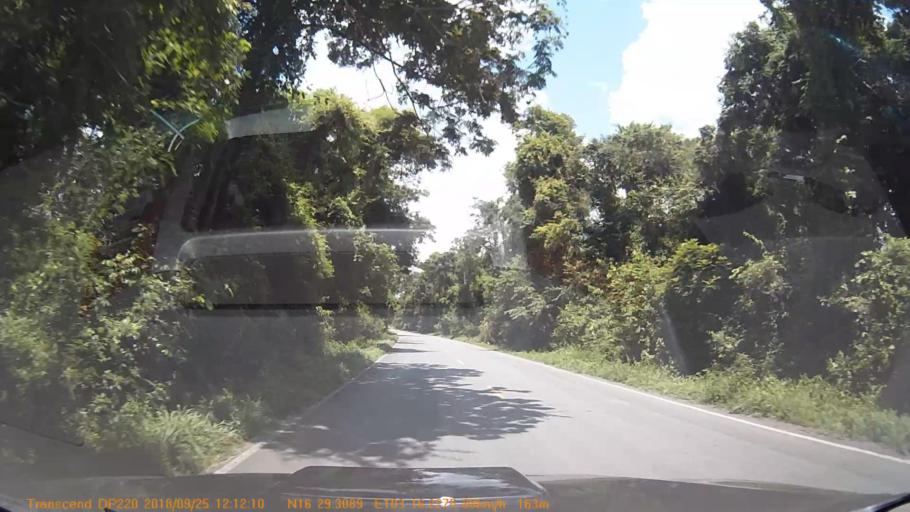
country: TH
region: Kalasin
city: Huai Mek
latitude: 16.4886
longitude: 103.2705
